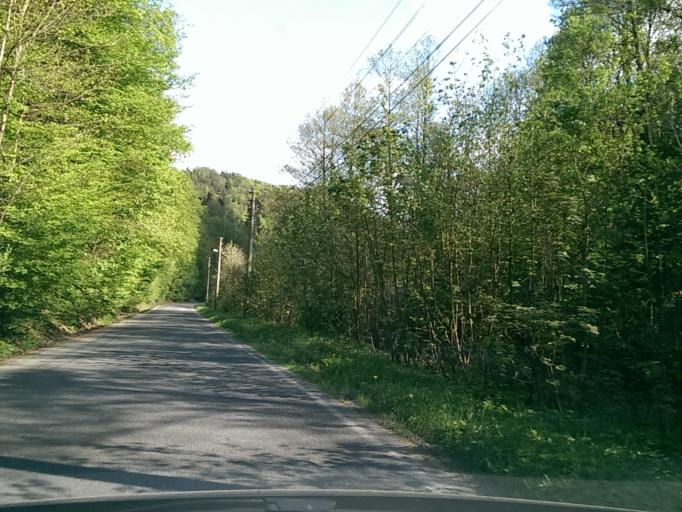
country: CZ
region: Liberecky
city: Mala Skala
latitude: 50.6576
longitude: 15.2157
